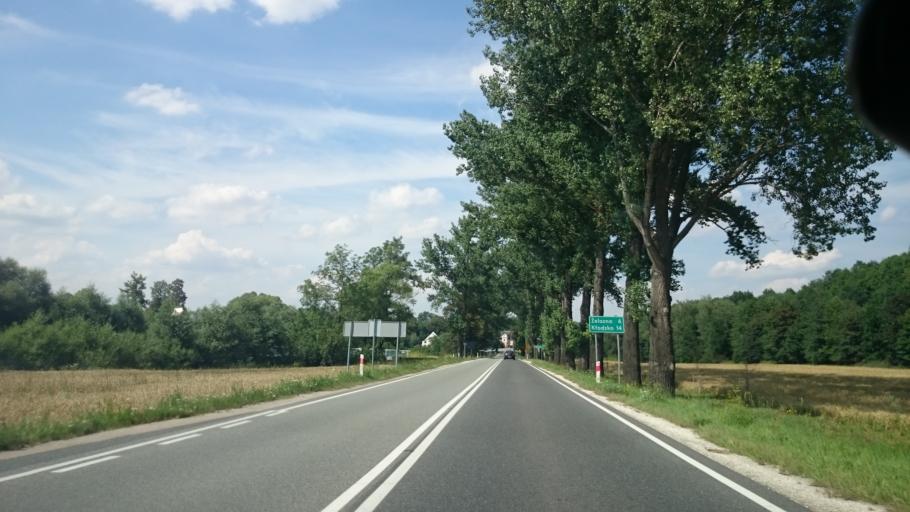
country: PL
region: Lower Silesian Voivodeship
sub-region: Powiat klodzki
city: Bystrzyca Klodzka
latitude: 50.3170
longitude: 16.6607
